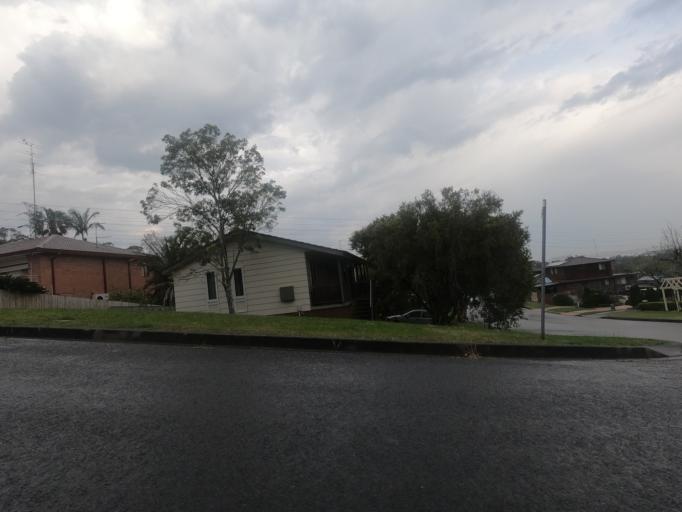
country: AU
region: New South Wales
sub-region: Wollongong
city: Koonawarra
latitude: -34.4921
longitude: 150.8089
